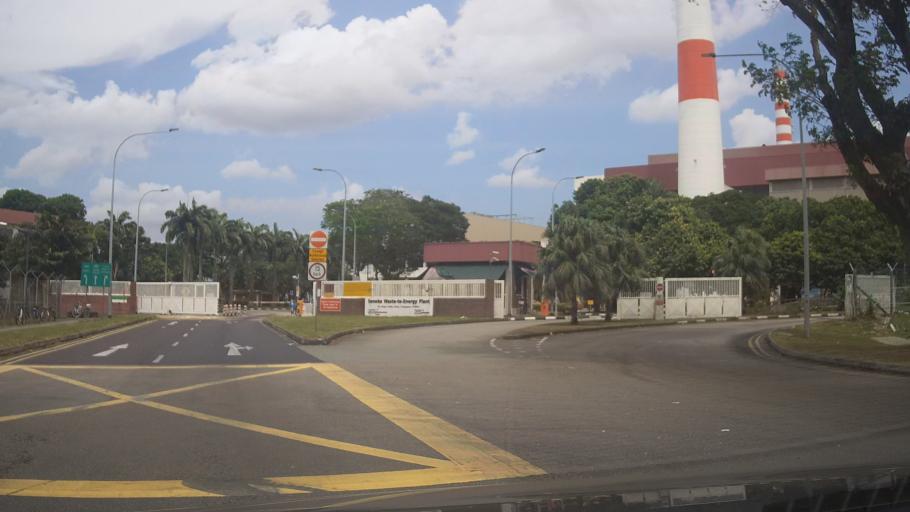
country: MY
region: Johor
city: Johor Bahru
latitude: 1.4610
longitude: 103.7933
